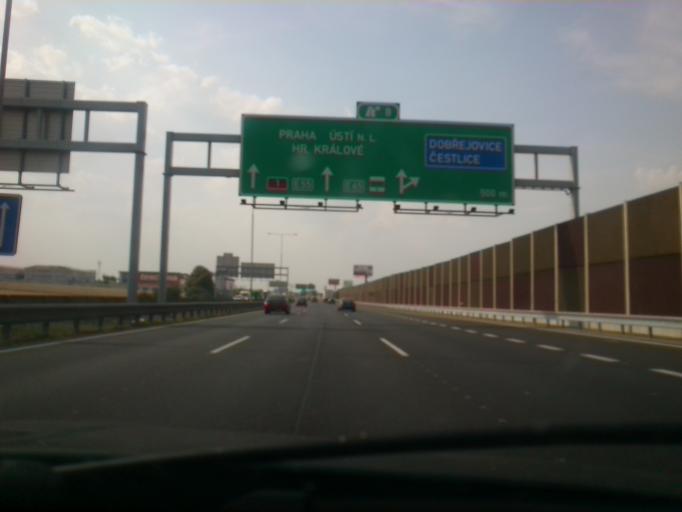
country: CZ
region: Central Bohemia
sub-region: Okres Praha-Zapad
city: Pruhonice
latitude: 49.9873
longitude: 14.5979
